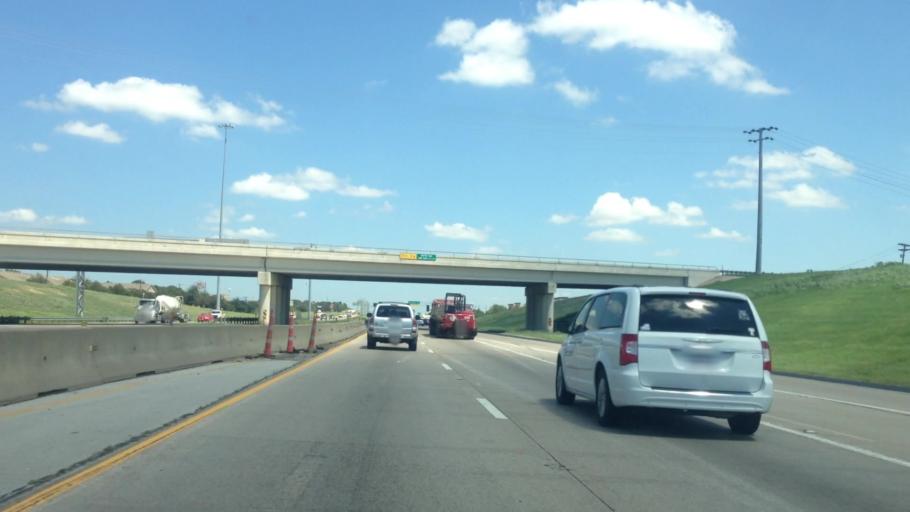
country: US
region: Texas
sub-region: Tarrant County
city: Bedford
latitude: 32.8438
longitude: -97.1163
